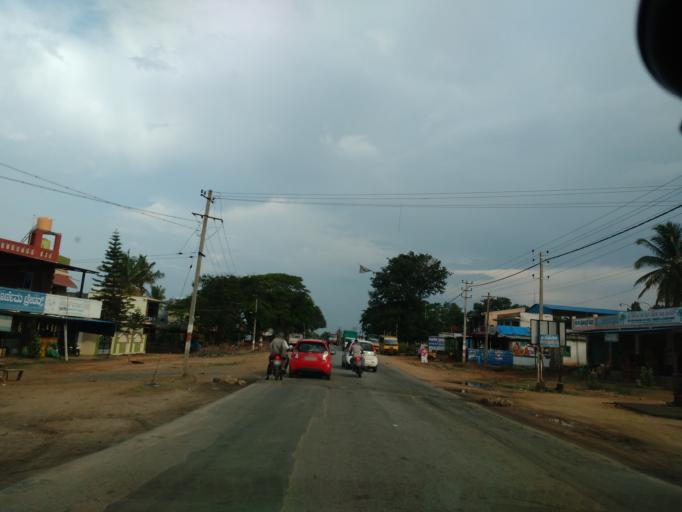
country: IN
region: Karnataka
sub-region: Hassan
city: Banavar
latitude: 13.4064
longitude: 76.1628
